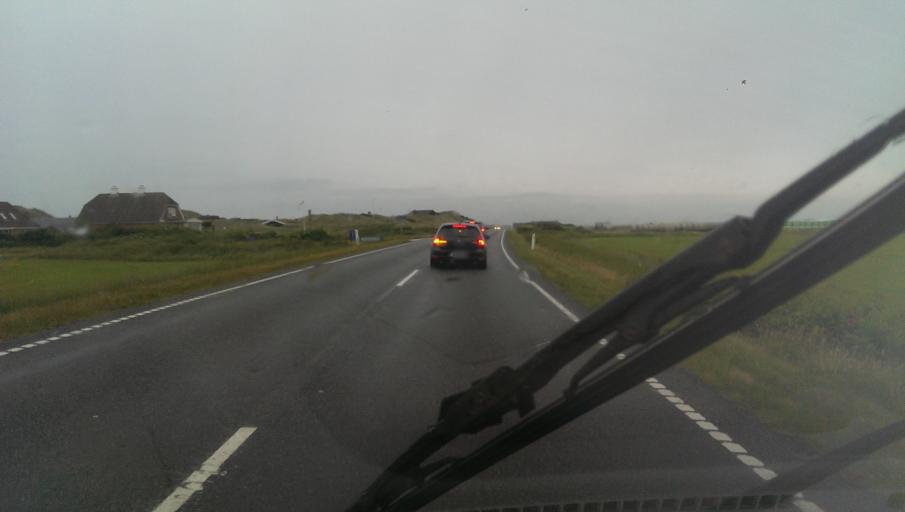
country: DK
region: Central Jutland
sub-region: Ringkobing-Skjern Kommune
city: Ringkobing
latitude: 56.1519
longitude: 8.1243
